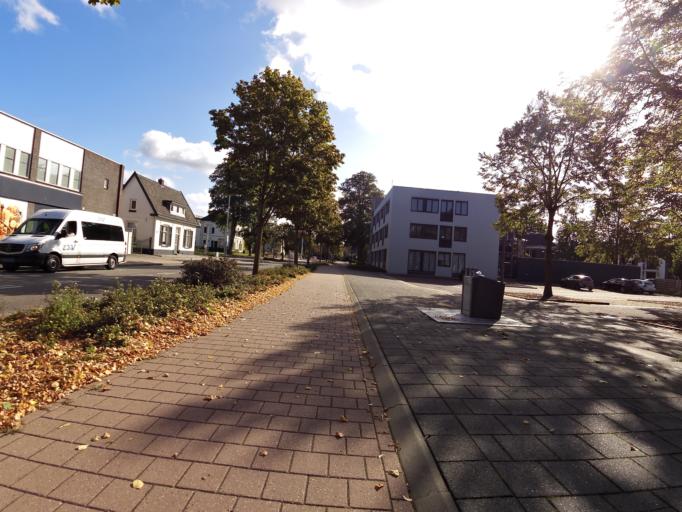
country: NL
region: Gelderland
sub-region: Gemeente Doetinchem
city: Doetinchem
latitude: 51.9662
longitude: 6.2965
